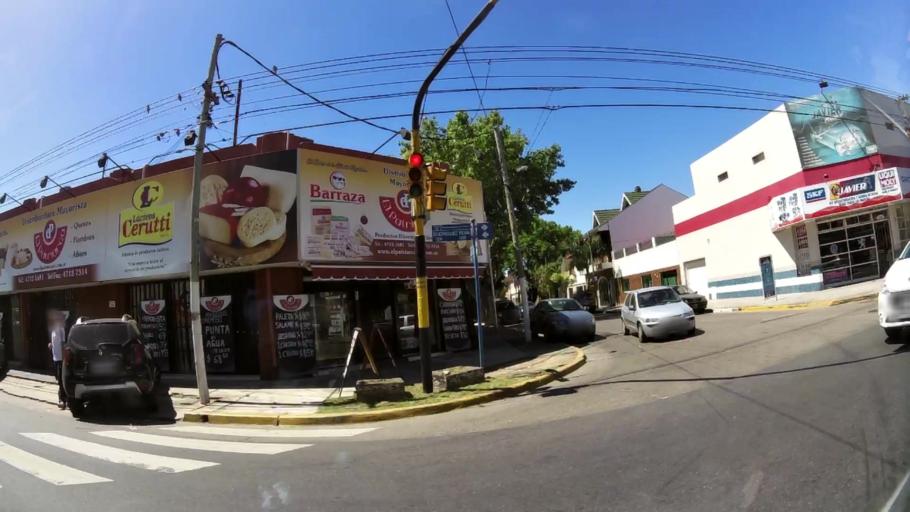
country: AR
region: Buenos Aires
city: Caseros
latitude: -34.5972
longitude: -58.5419
